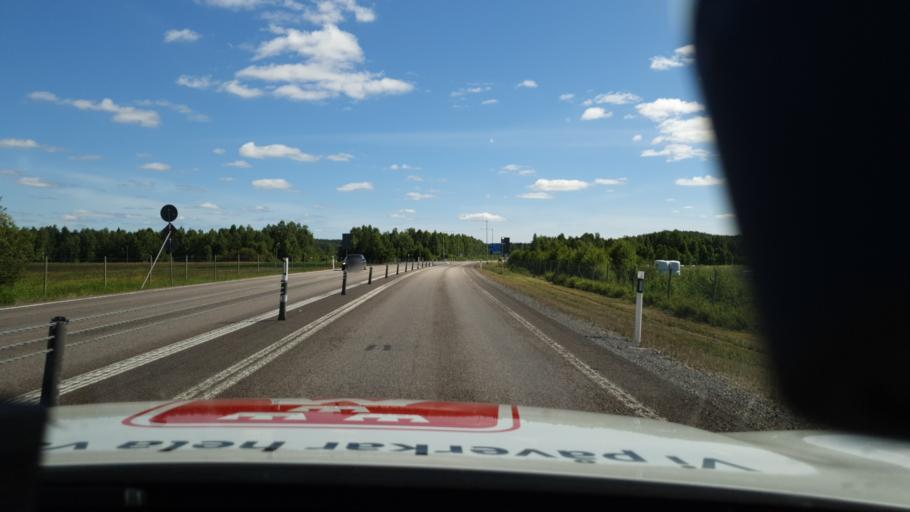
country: SE
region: Norrbotten
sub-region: Kalix Kommun
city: Rolfs
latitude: 65.8894
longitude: 22.9155
